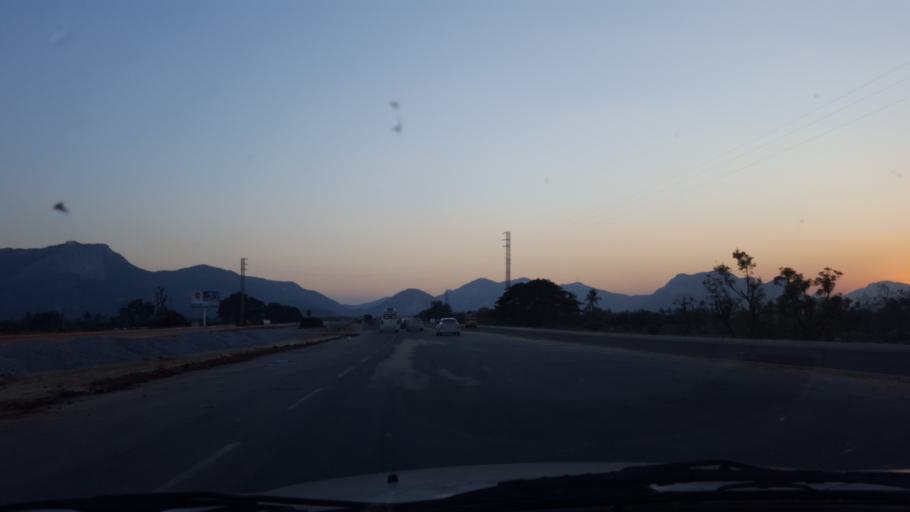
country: IN
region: Andhra Pradesh
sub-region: Chittoor
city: Narasingapuram
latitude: 13.5962
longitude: 79.3484
